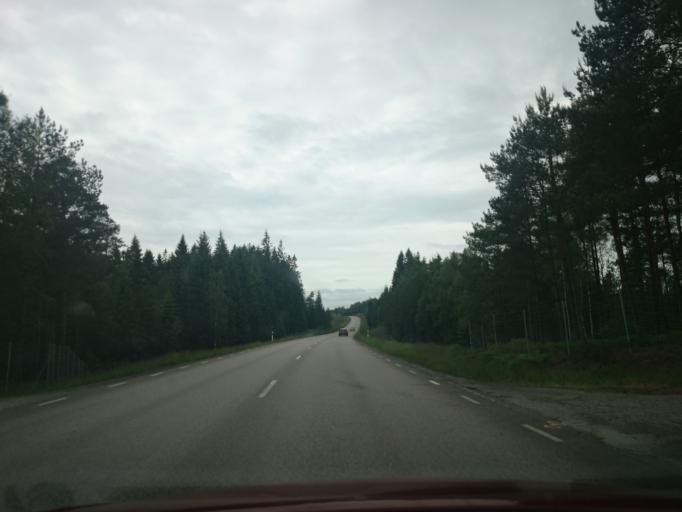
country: SE
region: Vaestra Goetaland
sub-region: Harryda Kommun
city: Hindas
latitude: 57.6847
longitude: 12.3666
